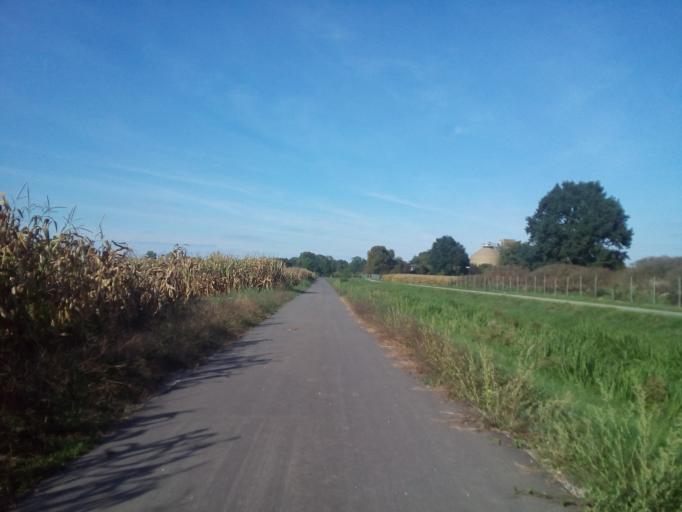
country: DE
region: Baden-Wuerttemberg
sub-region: Freiburg Region
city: Sasbach
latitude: 48.6624
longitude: 8.0730
